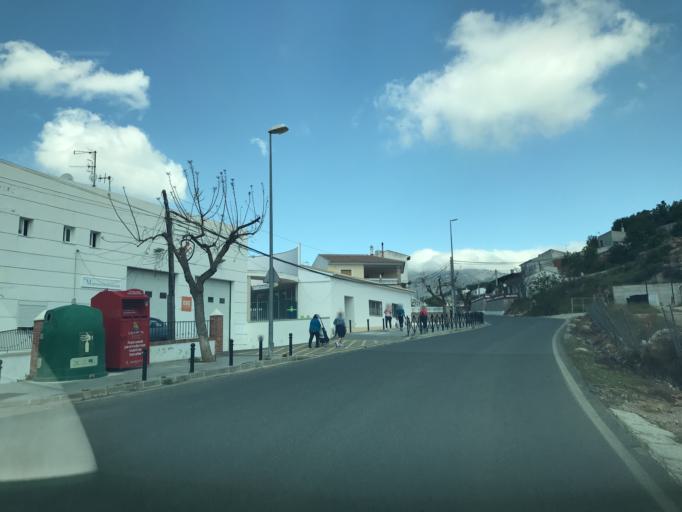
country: ES
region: Andalusia
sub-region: Provincia de Malaga
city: Periana
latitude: 36.9277
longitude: -4.1882
